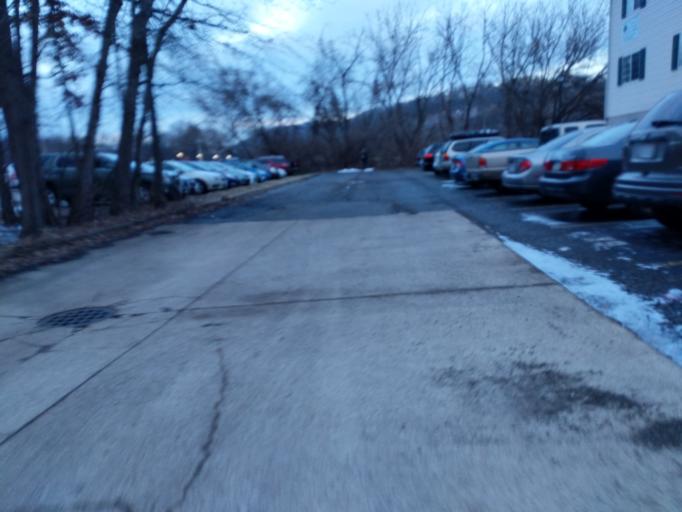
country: US
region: Ohio
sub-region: Athens County
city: Athens
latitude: 39.3289
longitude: -82.0933
